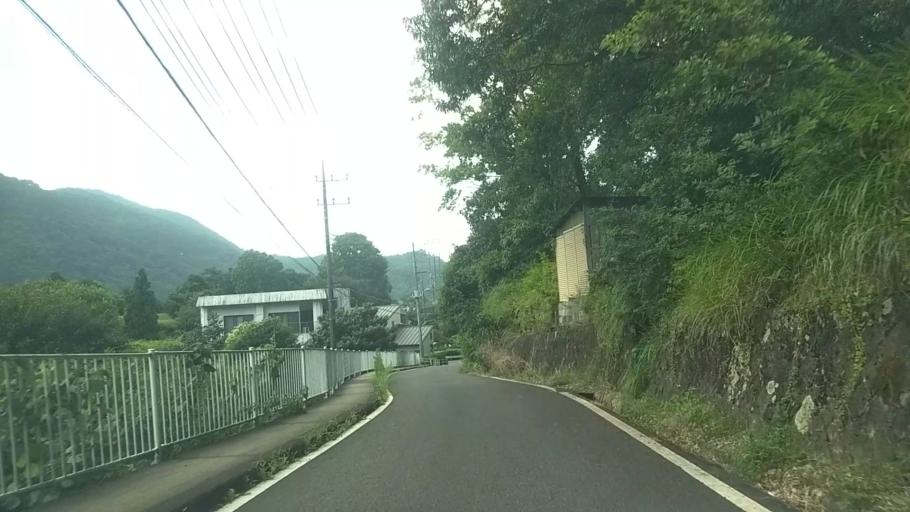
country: JP
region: Shizuoka
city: Mishima
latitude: 34.9987
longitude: 138.9444
